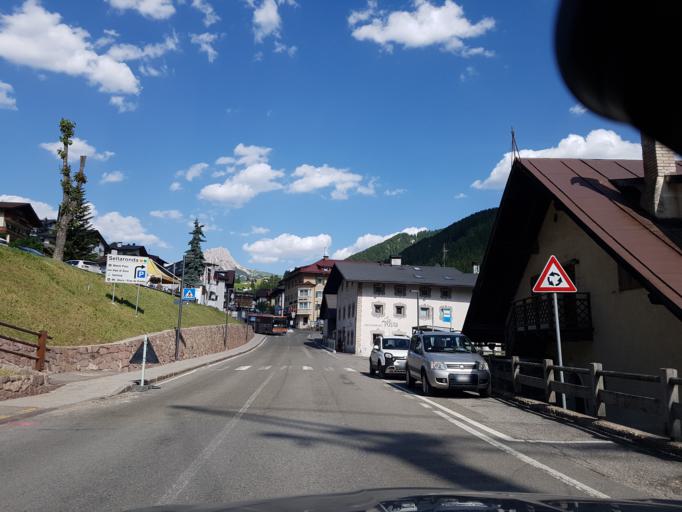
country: IT
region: Trentino-Alto Adige
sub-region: Bolzano
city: Santa Cristina Valgardena
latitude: 46.5581
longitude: 11.7211
